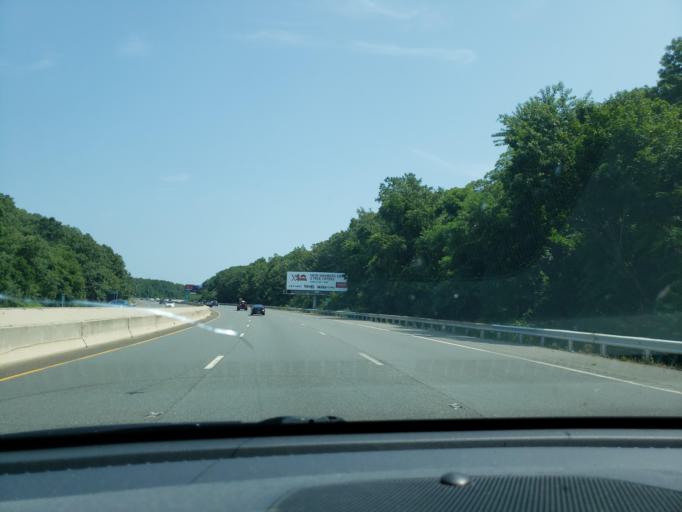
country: US
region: New Jersey
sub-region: Atlantic County
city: Pleasantville
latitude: 39.4059
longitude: -74.5385
